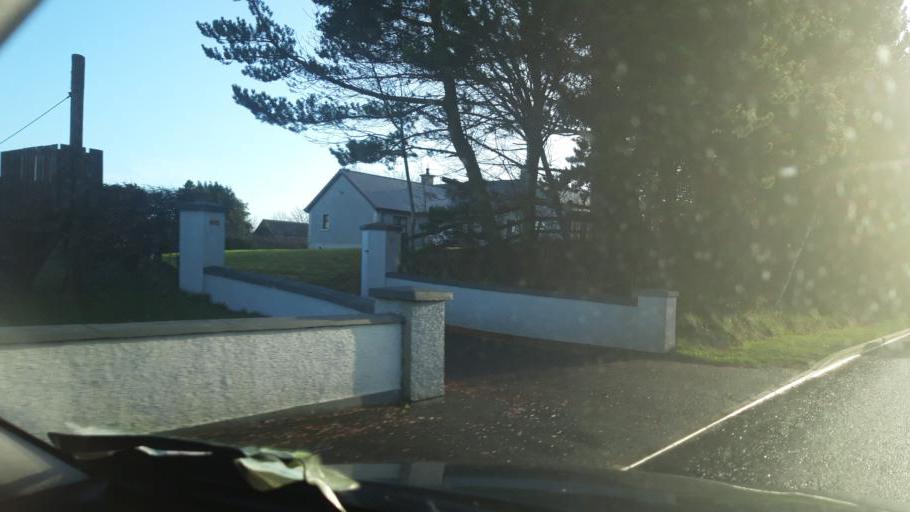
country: GB
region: Northern Ireland
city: Maghera
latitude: 54.9049
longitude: -6.6681
